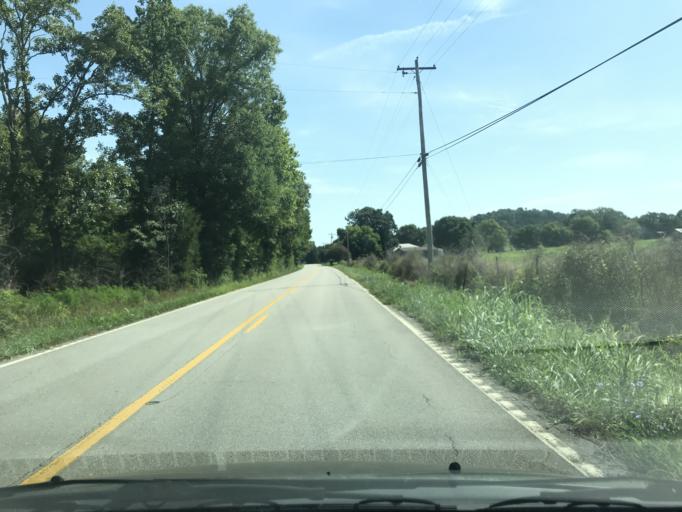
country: US
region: Tennessee
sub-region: Hamilton County
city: Sale Creek
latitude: 35.3211
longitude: -85.0214
